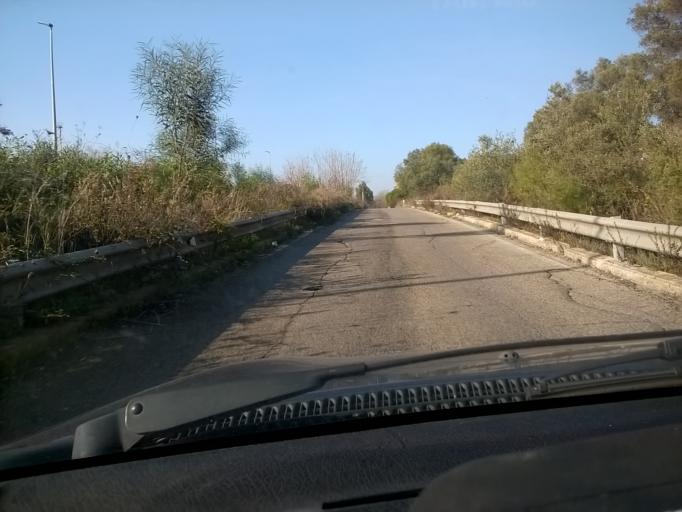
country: IT
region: Apulia
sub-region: Provincia di Taranto
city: Paolo VI
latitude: 40.4667
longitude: 17.2852
